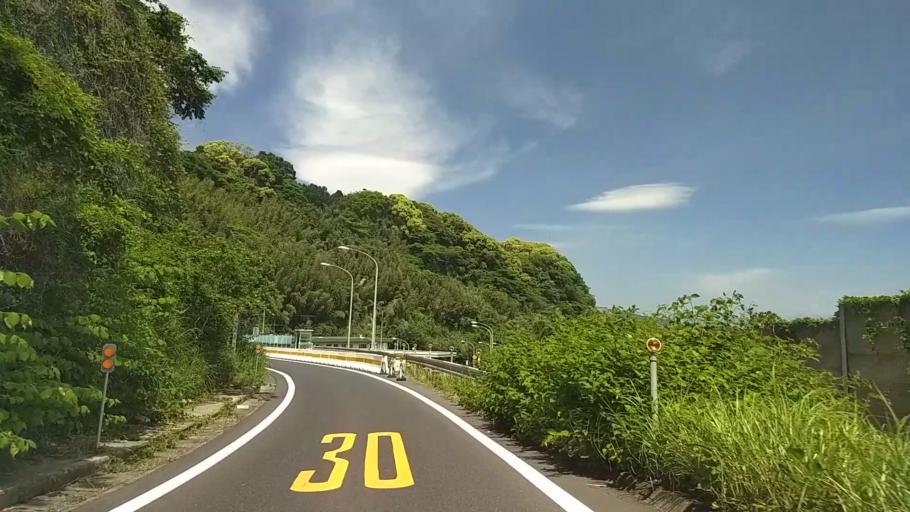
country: JP
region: Kanagawa
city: Yugawara
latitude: 35.1692
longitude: 139.1438
